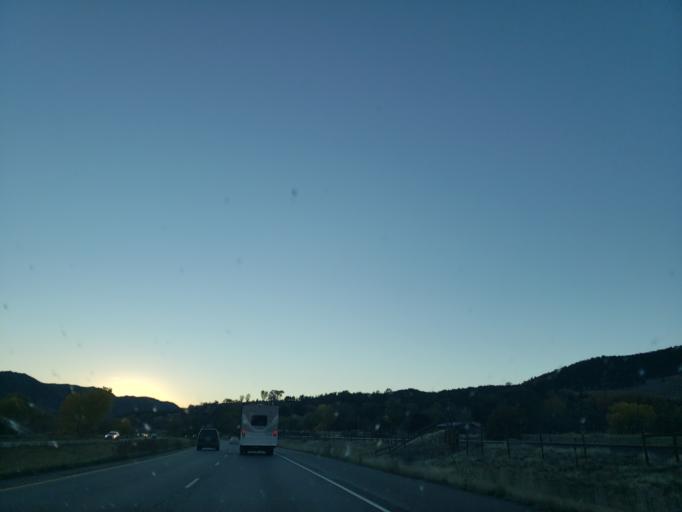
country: US
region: Colorado
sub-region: Garfield County
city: New Castle
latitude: 39.5737
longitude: -107.4711
